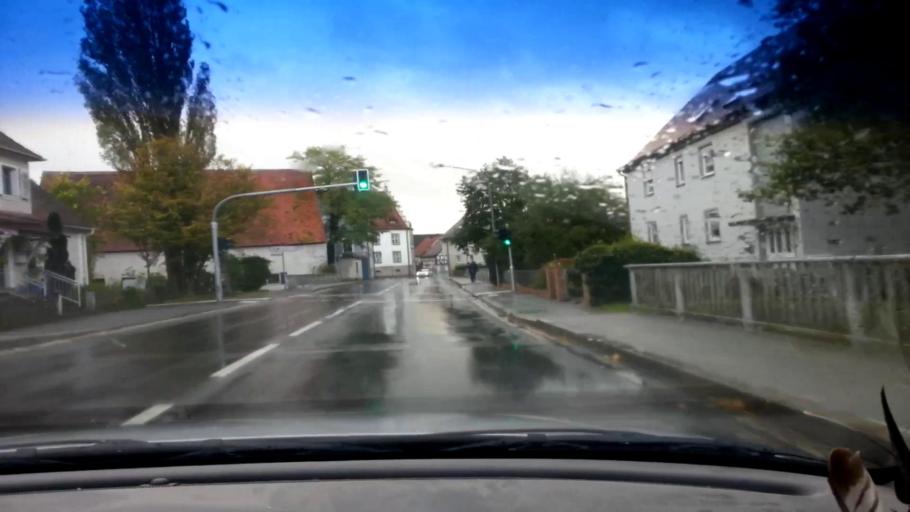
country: DE
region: Bavaria
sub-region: Upper Franconia
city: Burgebrach
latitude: 49.8305
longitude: 10.7423
